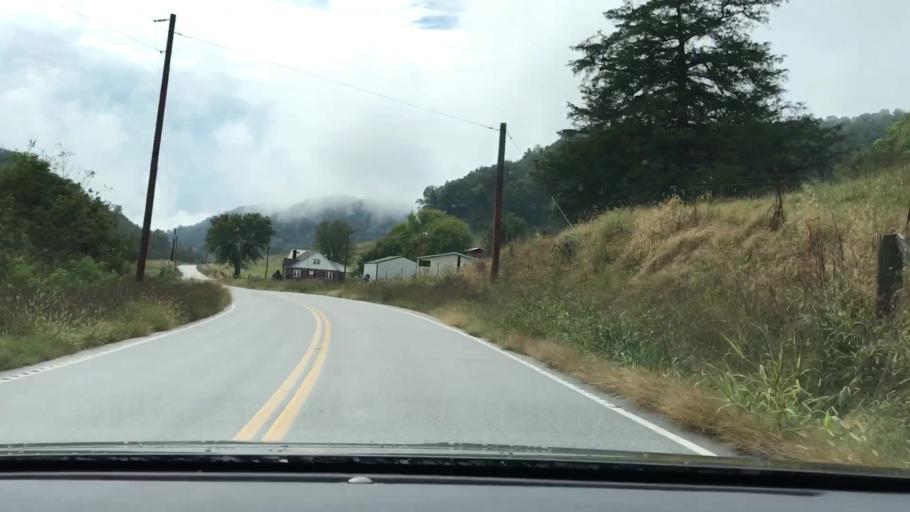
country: US
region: Tennessee
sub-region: Macon County
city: Lafayette
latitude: 36.4055
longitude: -85.9404
